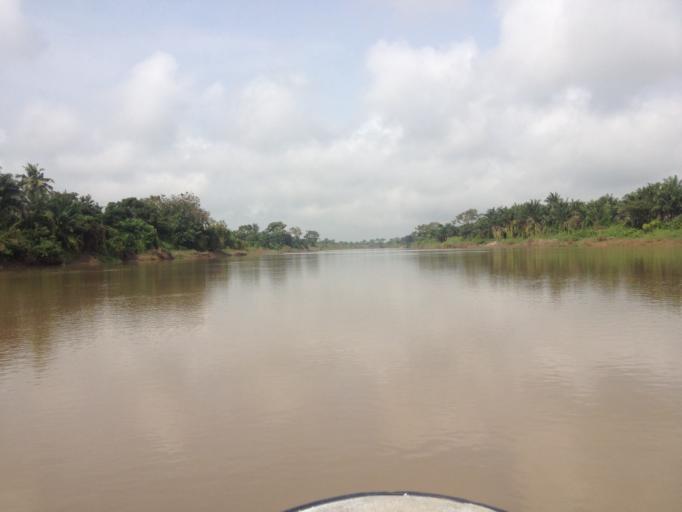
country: BJ
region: Mono
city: Come
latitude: 6.3838
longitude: 1.7832
